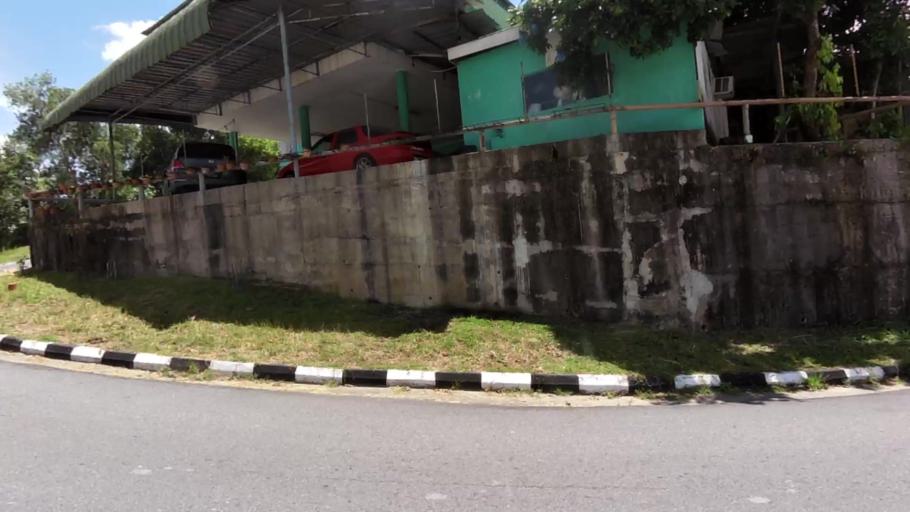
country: BN
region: Brunei and Muara
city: Bandar Seri Begawan
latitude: 4.9356
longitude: 114.9664
